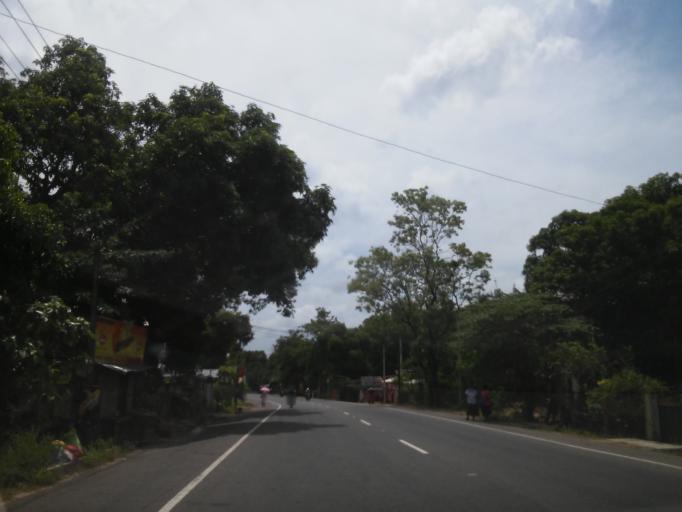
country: LK
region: Eastern Province
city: Trincomalee
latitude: 8.3729
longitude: 81.0063
